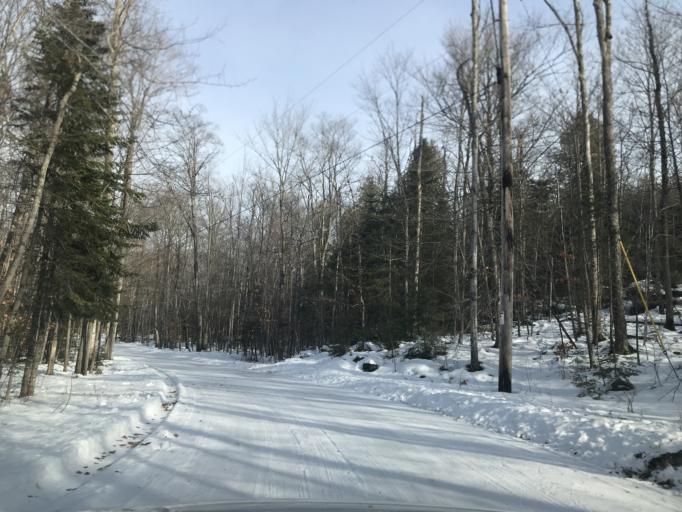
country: US
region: Wisconsin
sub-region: Door County
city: Sturgeon Bay
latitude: 45.1530
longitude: -87.0542
